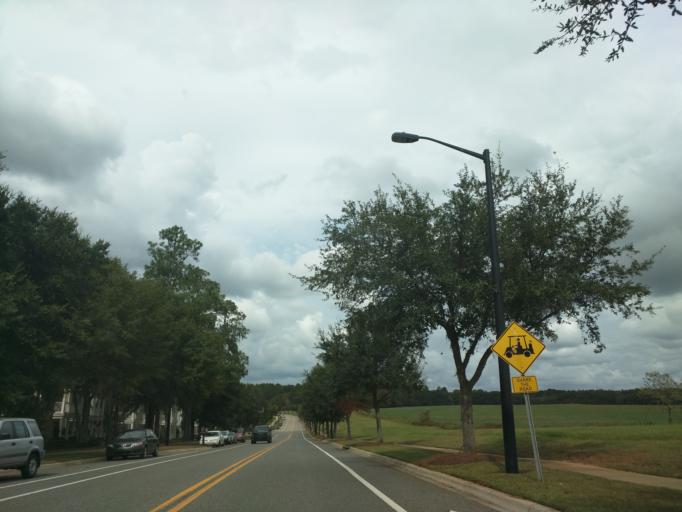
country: US
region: Florida
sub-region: Leon County
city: Tallahassee
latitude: 30.3993
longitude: -84.2093
